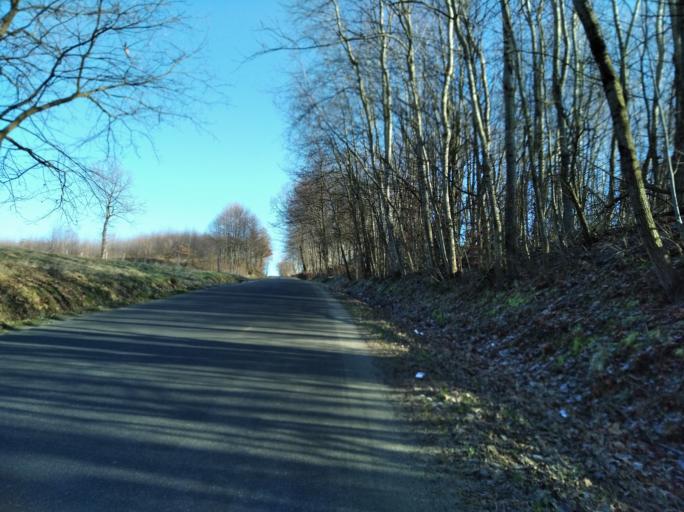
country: PL
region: Subcarpathian Voivodeship
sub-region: Powiat strzyzowski
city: Niebylec
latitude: 49.8558
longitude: 21.9196
